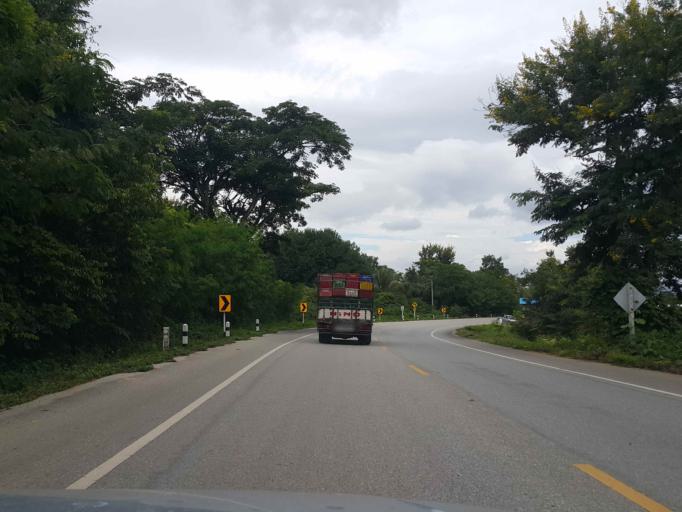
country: TH
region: Lamphun
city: Li
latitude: 17.7636
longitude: 98.9795
